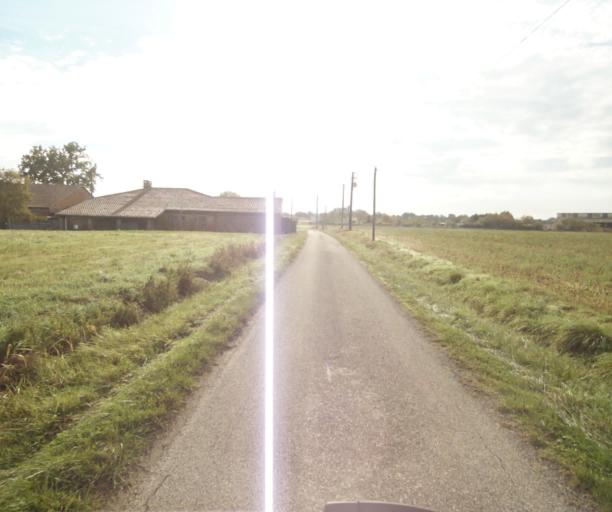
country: FR
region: Midi-Pyrenees
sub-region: Departement du Tarn-et-Garonne
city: Montech
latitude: 43.9795
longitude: 1.2445
